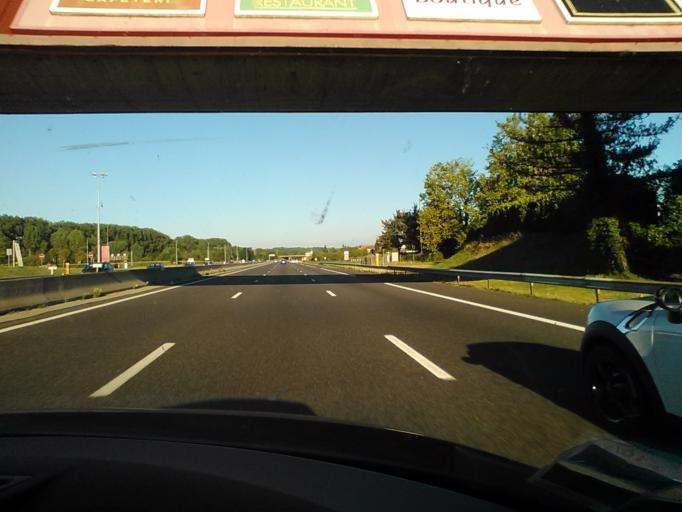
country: FR
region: Rhone-Alpes
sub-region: Departement de l'Isere
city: Saint-Alban-de-Roche
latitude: 45.6129
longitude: 5.2110
